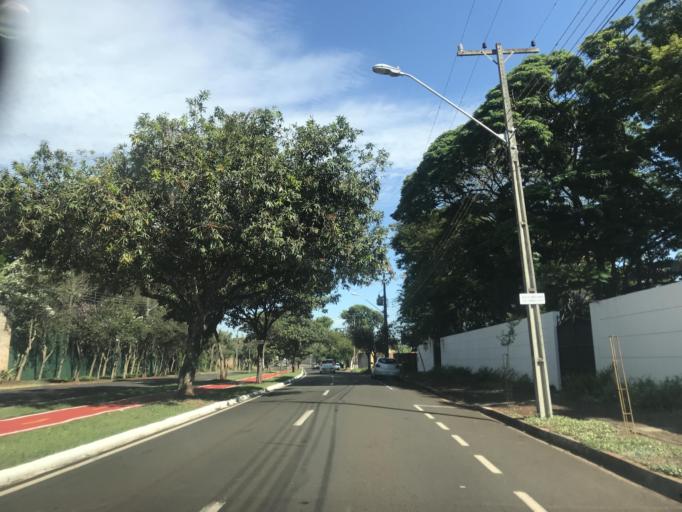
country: BR
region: Parana
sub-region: Londrina
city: Londrina
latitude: -23.3333
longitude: -51.1636
